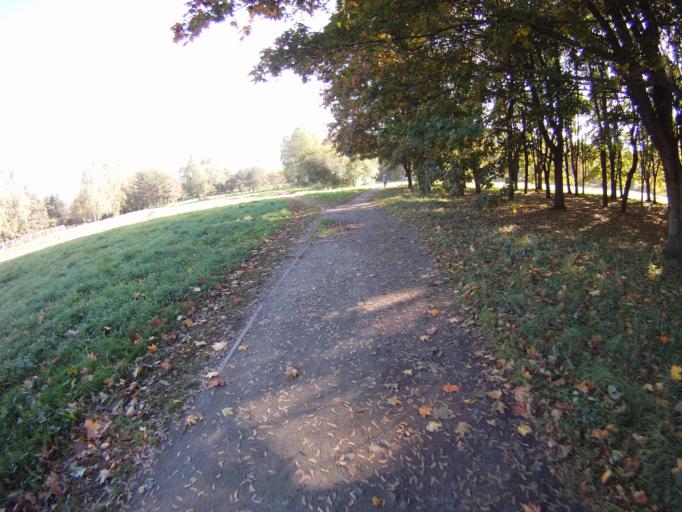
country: BY
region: Minsk
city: Minsk
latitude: 53.9343
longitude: 27.5707
